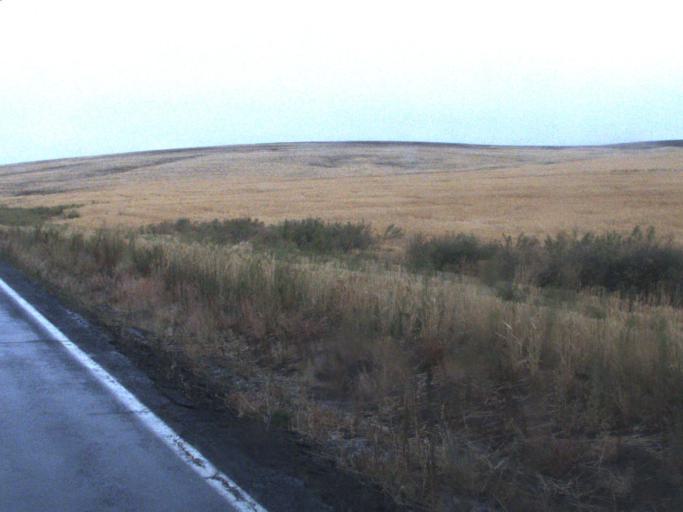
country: US
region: Washington
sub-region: Lincoln County
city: Davenport
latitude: 47.3782
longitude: -118.1236
